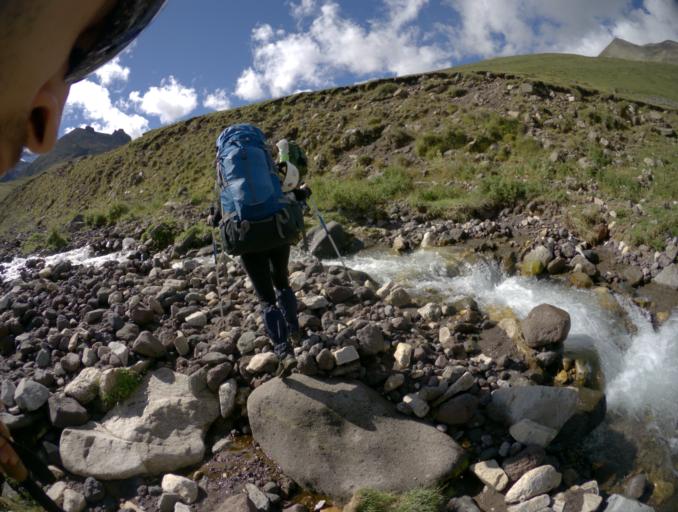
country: RU
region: Kabardino-Balkariya
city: Terskol
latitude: 43.4008
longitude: 42.3581
